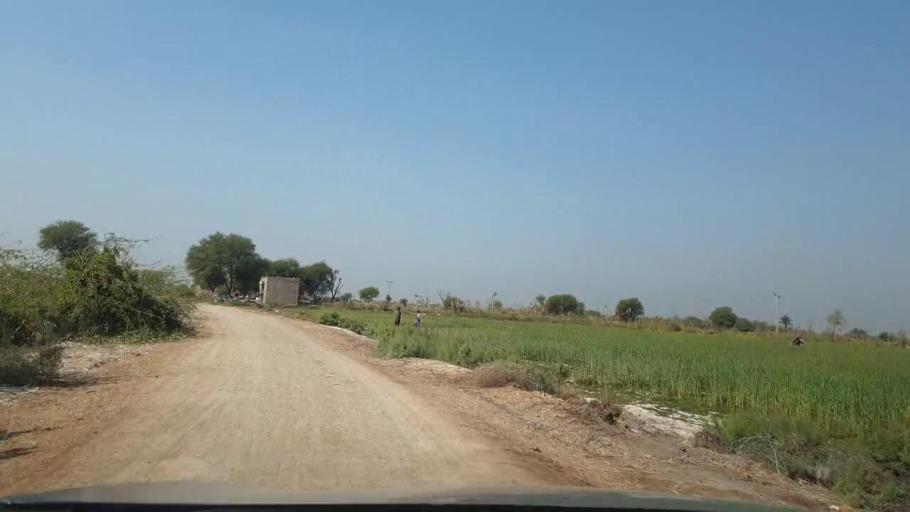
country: PK
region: Sindh
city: Berani
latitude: 25.7228
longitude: 68.8508
